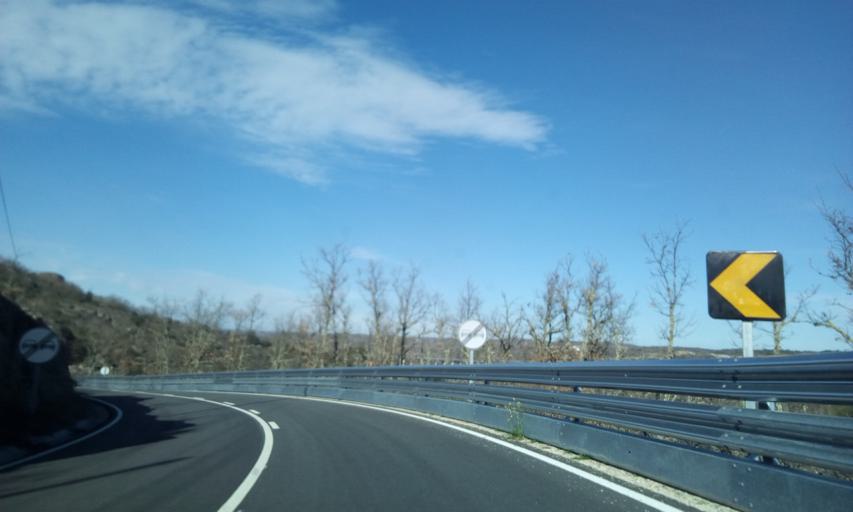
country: ES
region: Castille and Leon
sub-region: Provincia de Salamanca
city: Fuentes de Onoro
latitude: 40.6018
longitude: -6.9283
